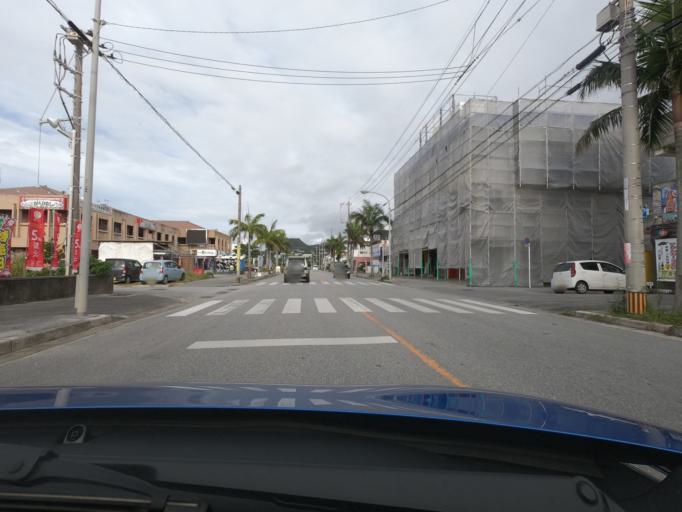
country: JP
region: Okinawa
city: Nago
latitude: 26.6572
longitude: 127.8849
